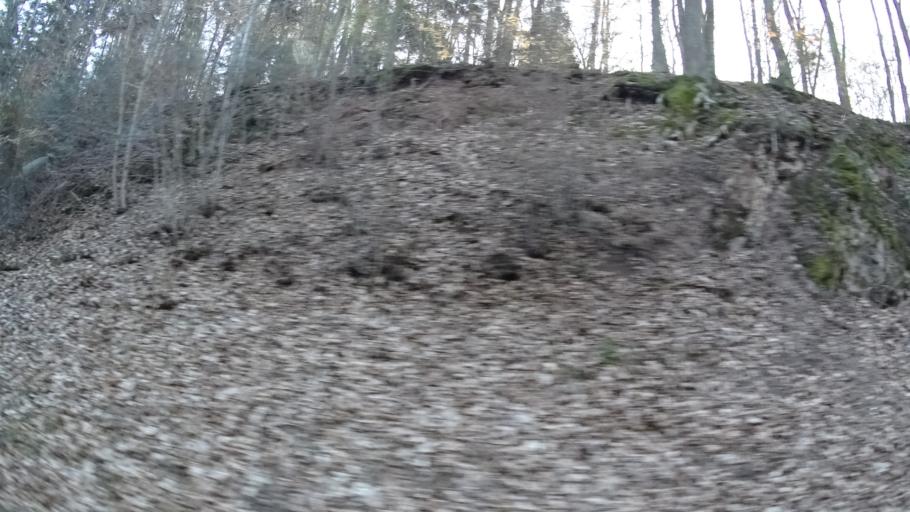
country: DE
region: Rheinland-Pfalz
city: Wurzweiler
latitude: 49.6370
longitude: 7.8730
